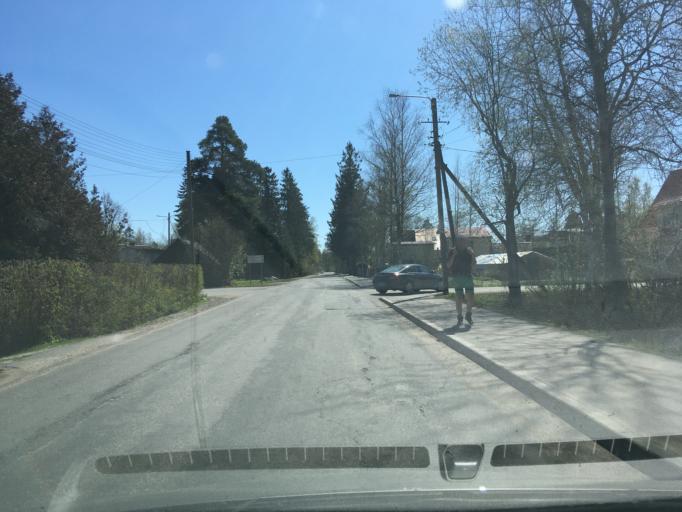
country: EE
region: Harju
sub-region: Raasiku vald
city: Arukula
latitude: 59.3695
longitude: 25.0789
